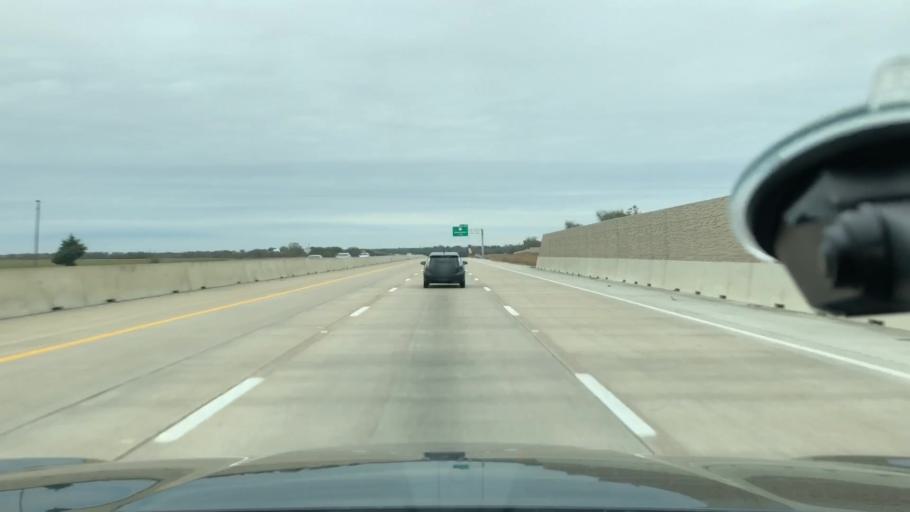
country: US
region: Texas
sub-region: Ellis County
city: Waxahachie
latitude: 32.3377
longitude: -96.8568
